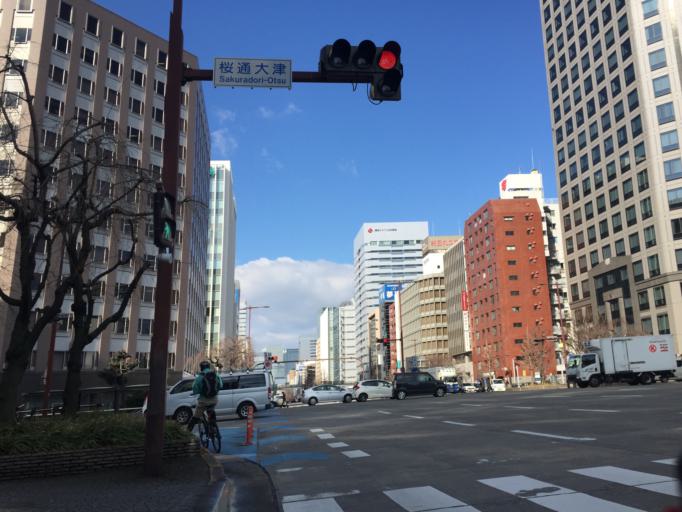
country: JP
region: Aichi
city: Nagoya-shi
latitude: 35.1736
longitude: 136.9068
